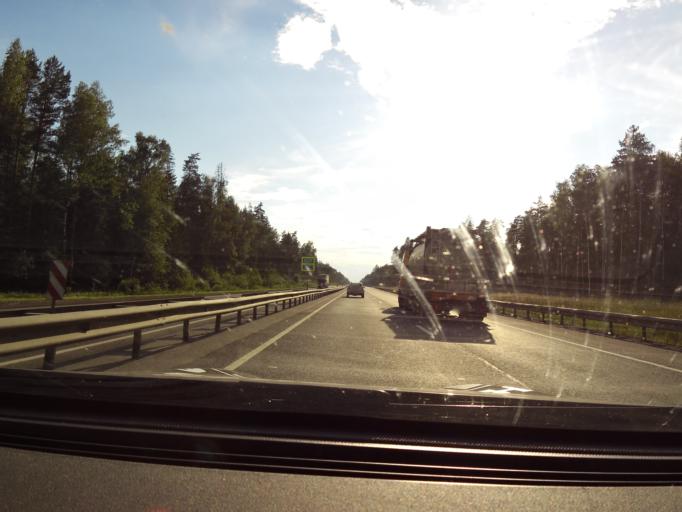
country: RU
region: Vladimir
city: Krasnyy Oktyabr'
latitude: 56.2165
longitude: 41.4162
